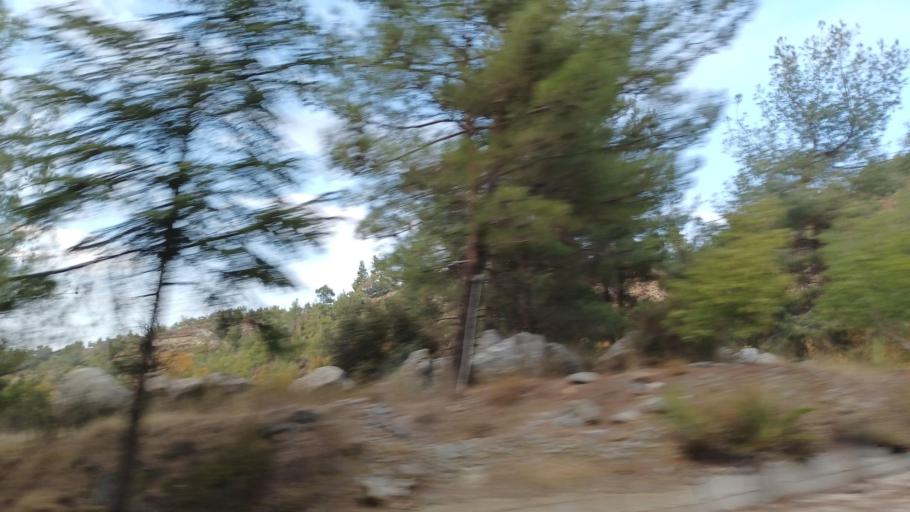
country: CY
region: Lefkosia
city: Kakopetria
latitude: 34.9734
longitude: 32.9141
